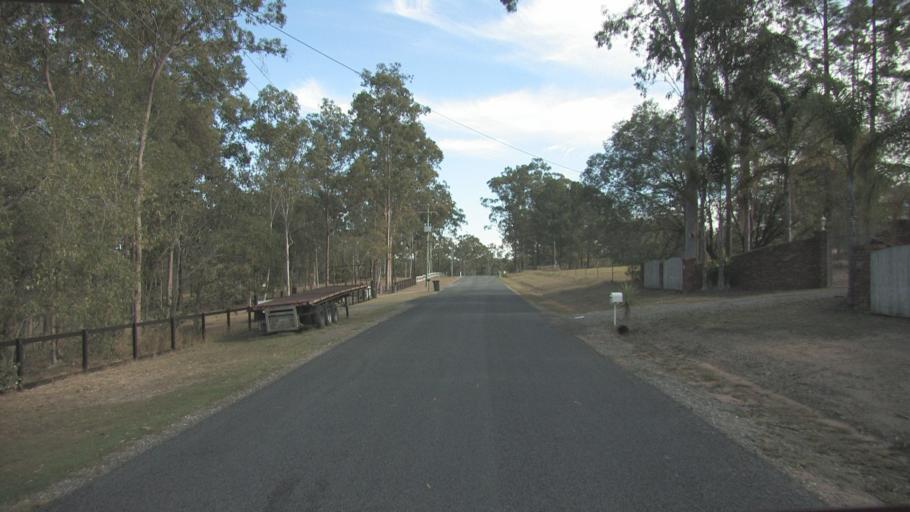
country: AU
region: Queensland
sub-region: Logan
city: North Maclean
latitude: -27.7785
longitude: 152.9728
